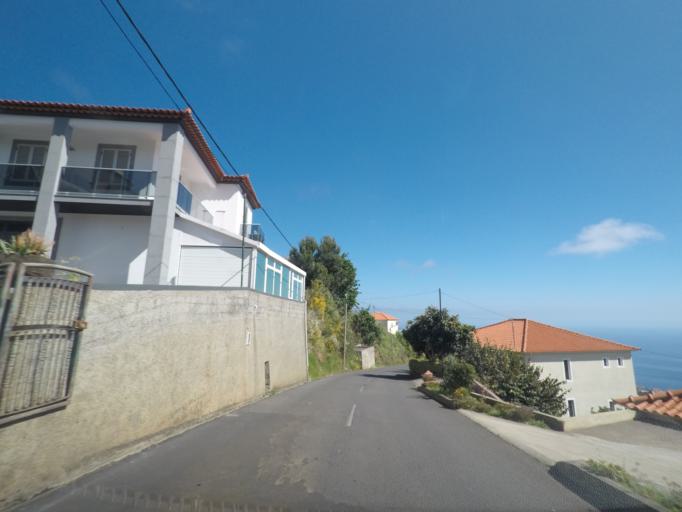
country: PT
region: Madeira
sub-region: Calheta
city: Arco da Calheta
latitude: 32.7045
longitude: -17.1123
